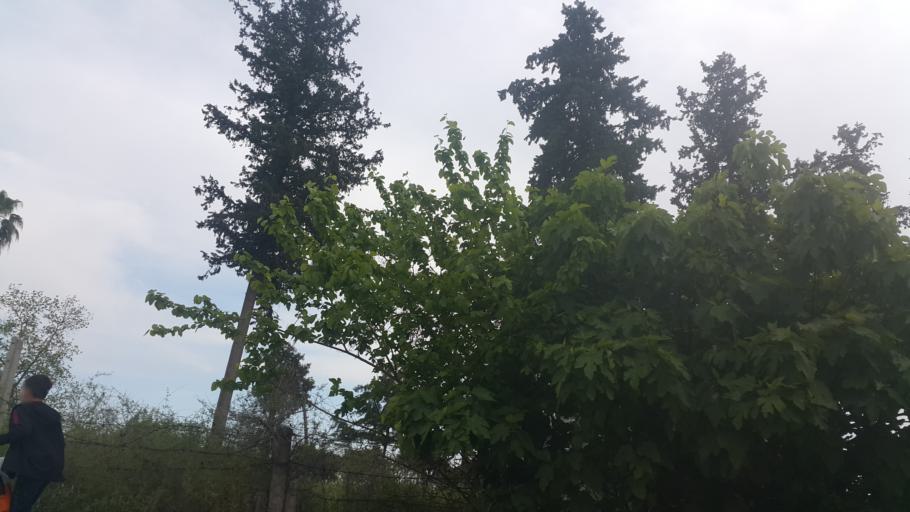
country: TR
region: Mersin
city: Tarsus
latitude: 36.9186
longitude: 34.9134
